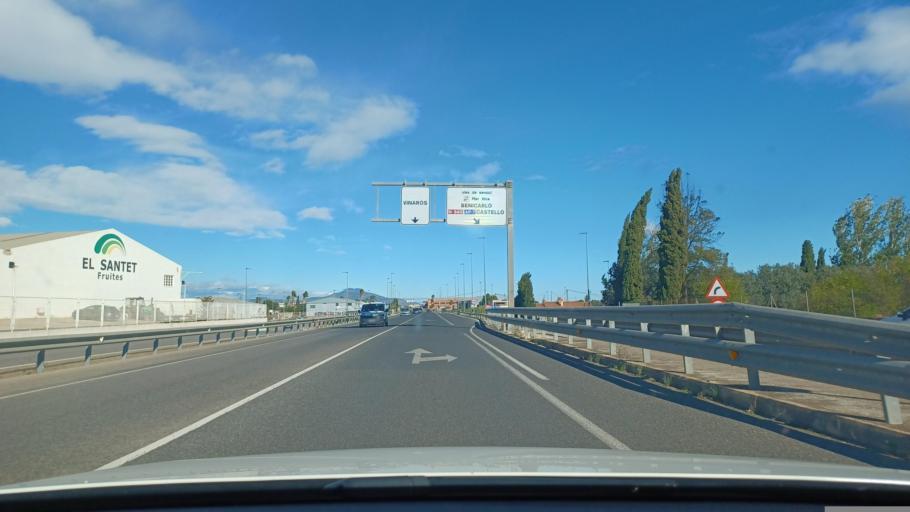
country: ES
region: Valencia
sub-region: Provincia de Castello
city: Benicarlo
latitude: 40.4305
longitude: 0.4364
